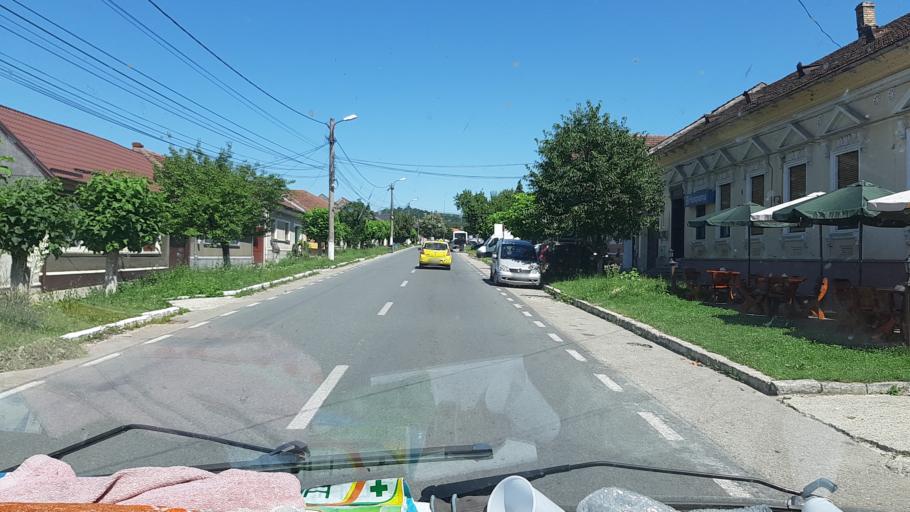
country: RO
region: Caras-Severin
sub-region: Oras Bocsa
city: Bocsa
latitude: 45.3798
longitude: 21.7672
